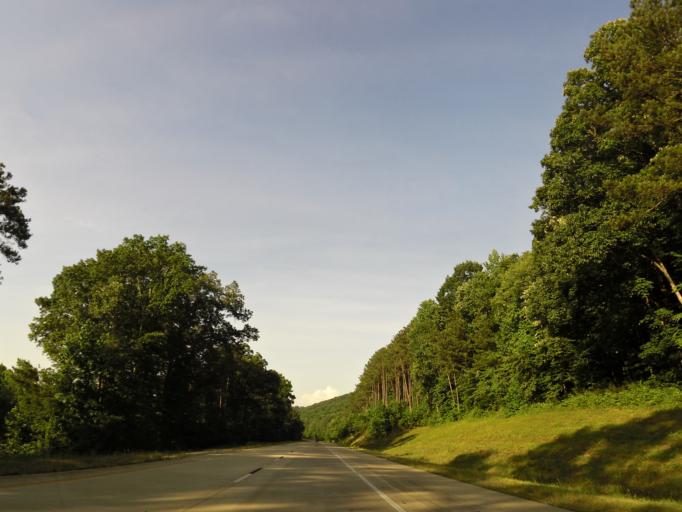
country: US
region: Alabama
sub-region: Etowah County
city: Attalla
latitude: 34.0486
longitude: -86.0507
